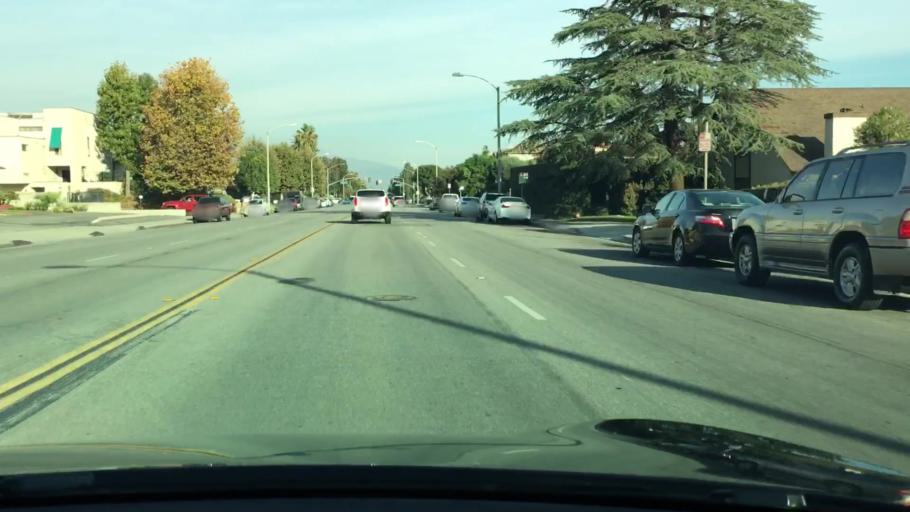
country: US
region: California
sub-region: Los Angeles County
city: Temple City
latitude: 34.1243
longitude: -118.0671
